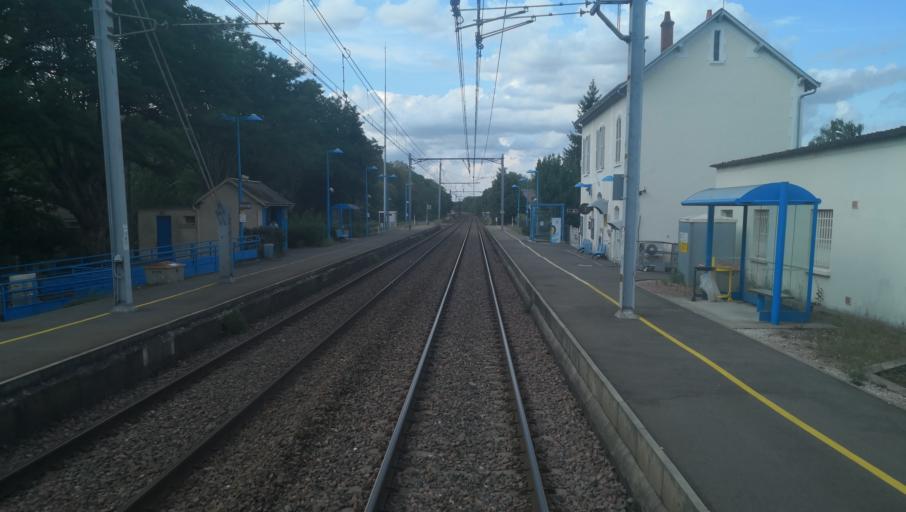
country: FR
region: Centre
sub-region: Departement du Loiret
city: Saint-Cyr-en-Val
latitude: 47.8189
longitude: 1.9474
